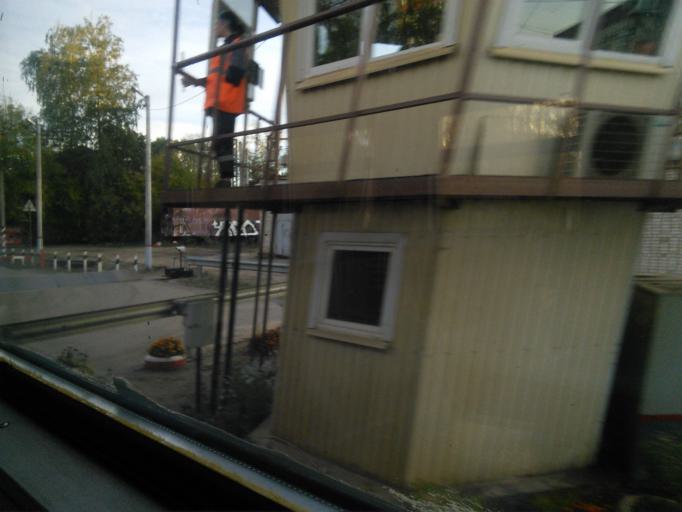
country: RU
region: Moscow
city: Mar'ina Roshcha
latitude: 55.8099
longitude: 37.6155
